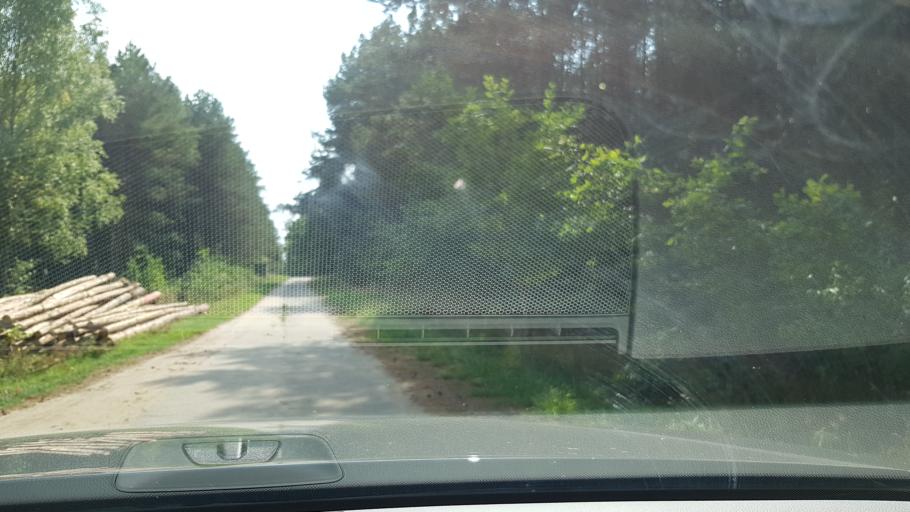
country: DE
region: Brandenburg
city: Rheinsberg
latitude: 53.0622
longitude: 12.9500
